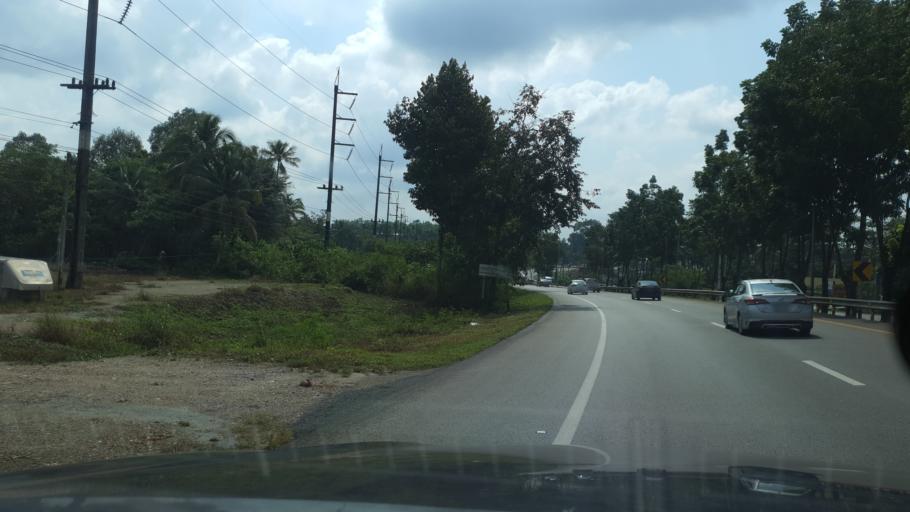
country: TH
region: Chumphon
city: Chumphon
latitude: 10.5418
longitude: 99.1166
